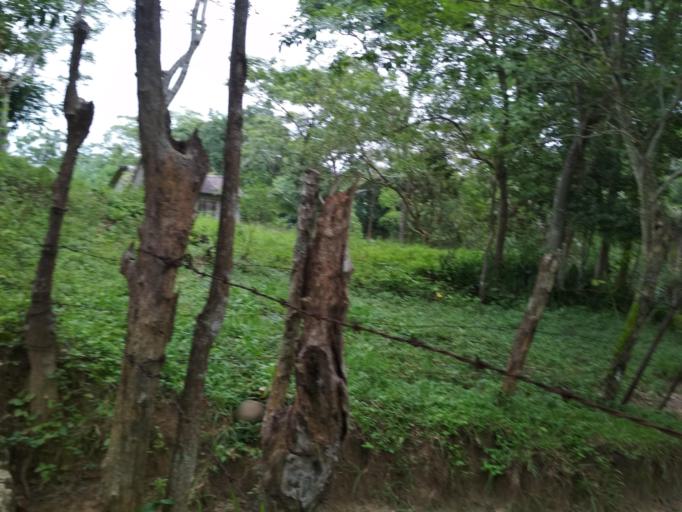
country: MX
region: Veracruz
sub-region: San Andres Tuxtla
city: Soyata
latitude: 18.3974
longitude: -95.3205
